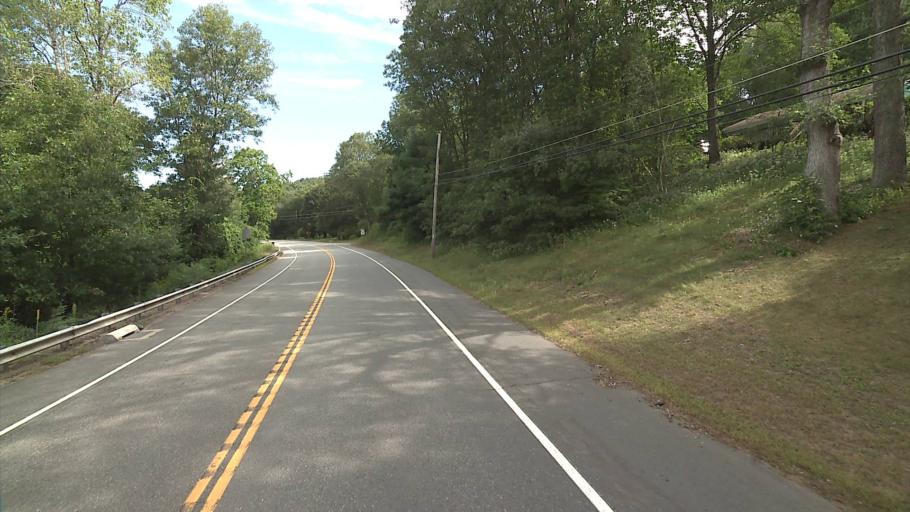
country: US
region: Connecticut
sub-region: Tolland County
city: Storrs
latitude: 41.8316
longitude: -72.3064
